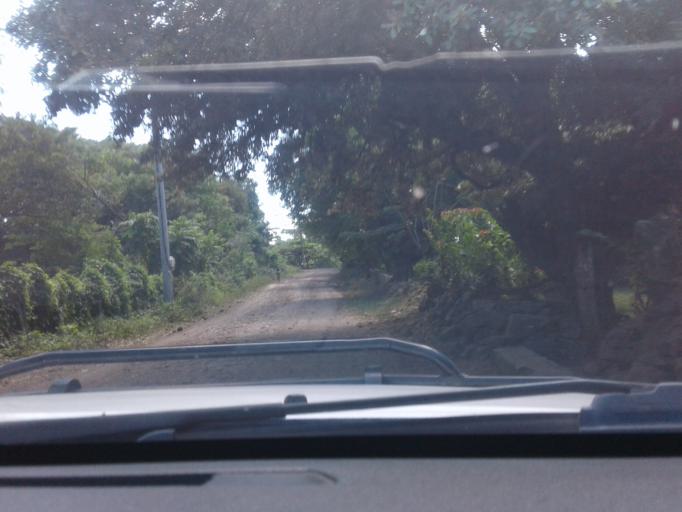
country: NI
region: Rivas
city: Altagracia
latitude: 11.4456
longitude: -85.5618
